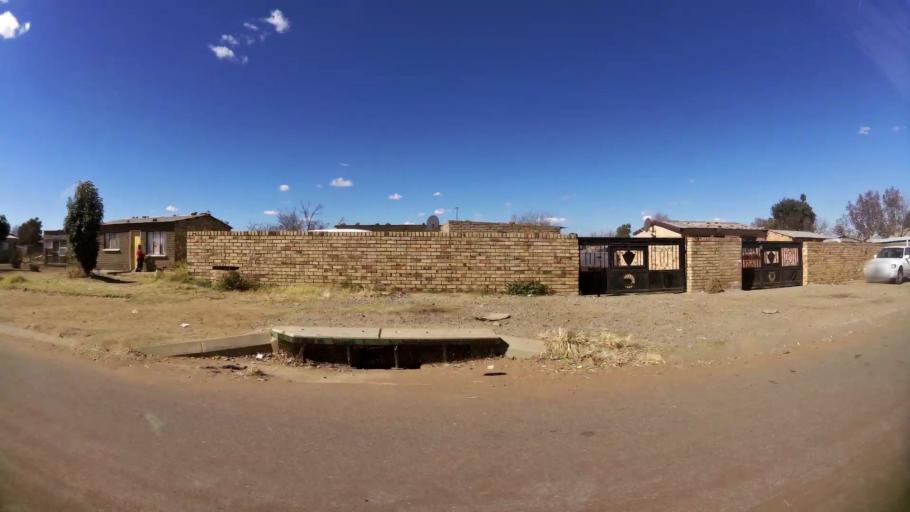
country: ZA
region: North-West
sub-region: Dr Kenneth Kaunda District Municipality
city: Klerksdorp
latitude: -26.8709
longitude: 26.5750
